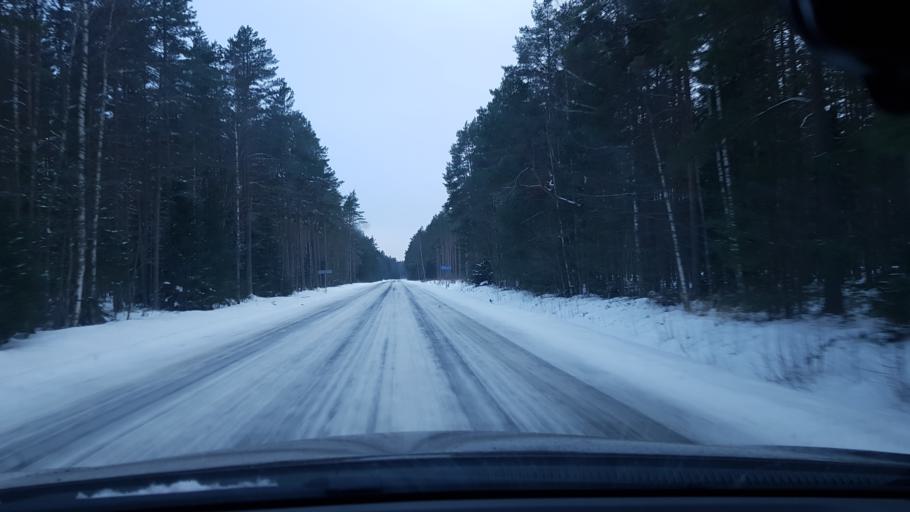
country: EE
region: Harju
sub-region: Loksa linn
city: Loksa
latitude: 59.5559
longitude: 25.8205
